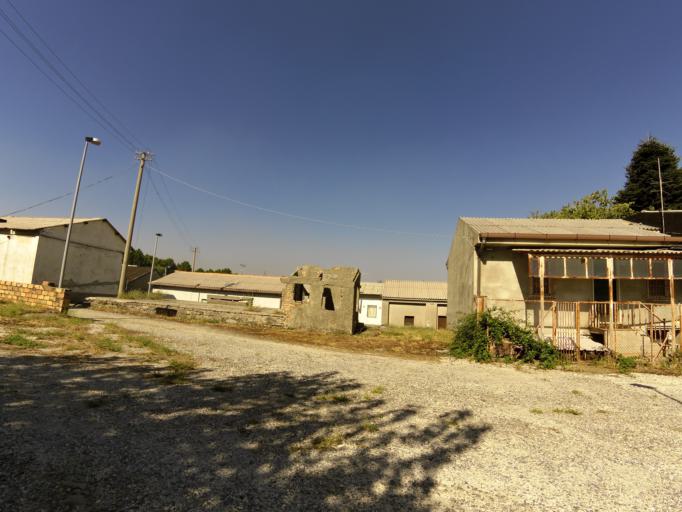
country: IT
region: Calabria
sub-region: Provincia di Vibo-Valentia
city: Nardodipace
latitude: 38.4748
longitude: 16.3963
